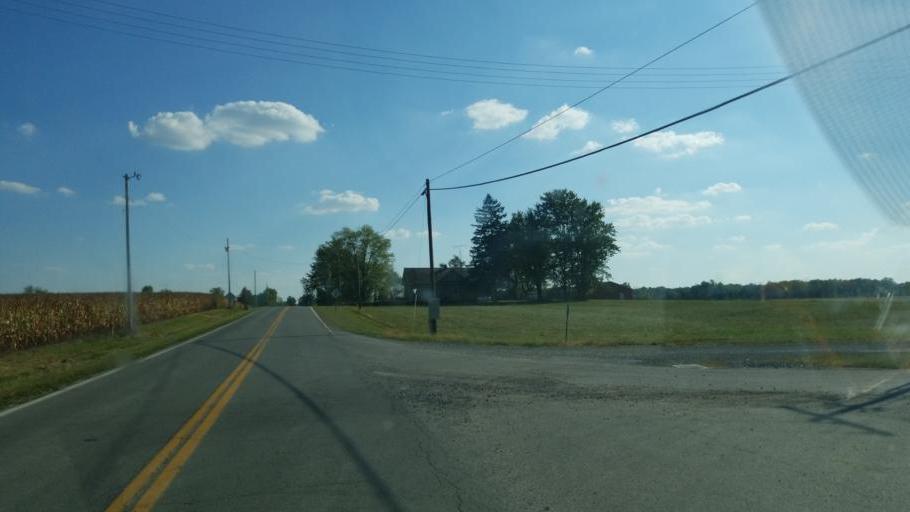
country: US
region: Ohio
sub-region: Hardin County
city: Forest
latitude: 40.6423
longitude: -83.3809
